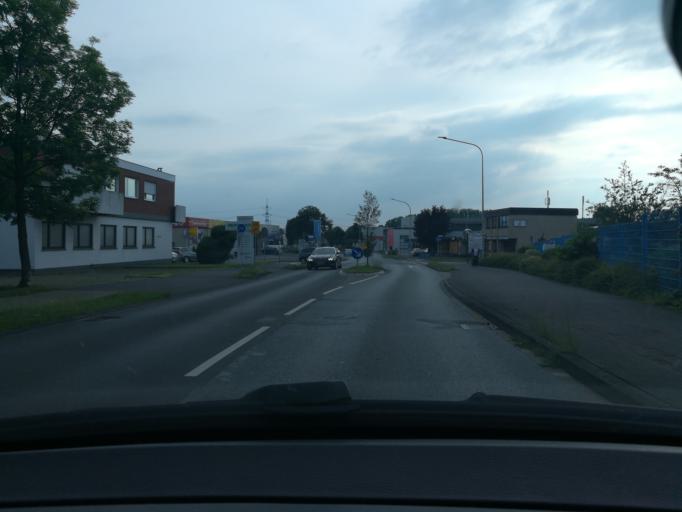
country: DE
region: North Rhine-Westphalia
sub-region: Regierungsbezirk Detmold
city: Oerlinghausen
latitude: 51.9053
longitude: 8.6421
